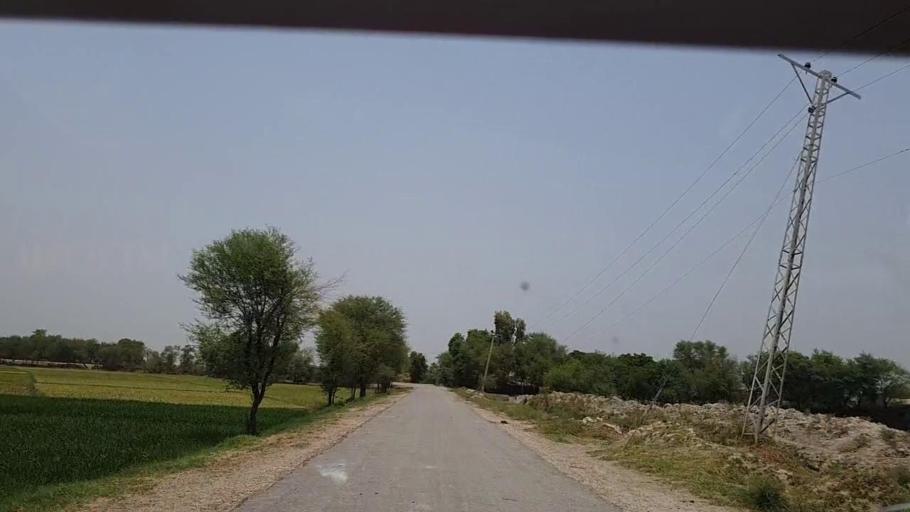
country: PK
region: Sindh
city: Khairpur Nathan Shah
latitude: 27.0206
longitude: 67.6693
